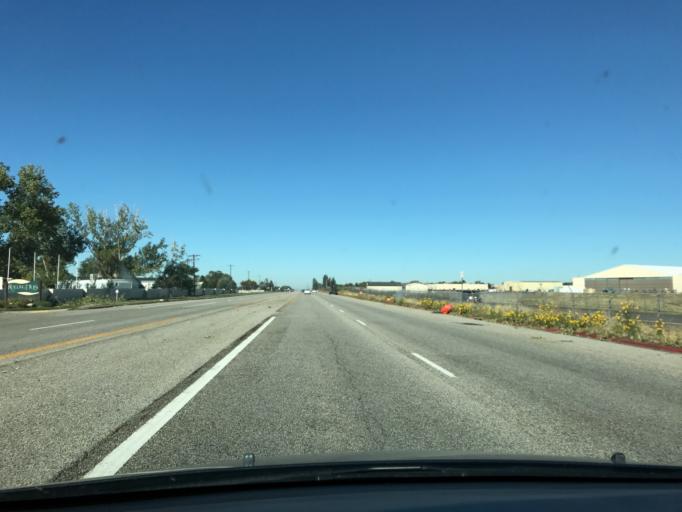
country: US
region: Utah
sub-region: Davis County
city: Hill Air Force Bace
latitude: 41.1036
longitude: -111.9641
